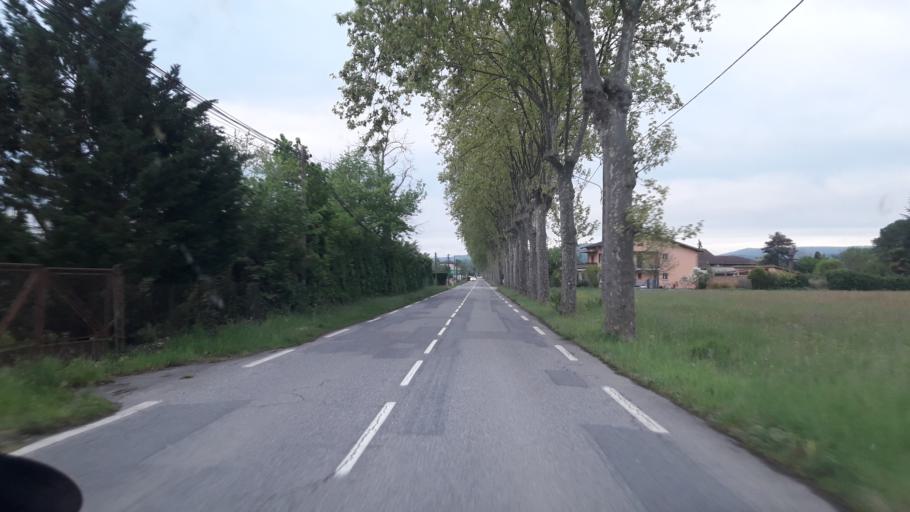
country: FR
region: Midi-Pyrenees
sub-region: Departement de la Haute-Garonne
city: Cazeres
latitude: 43.2239
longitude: 1.0847
